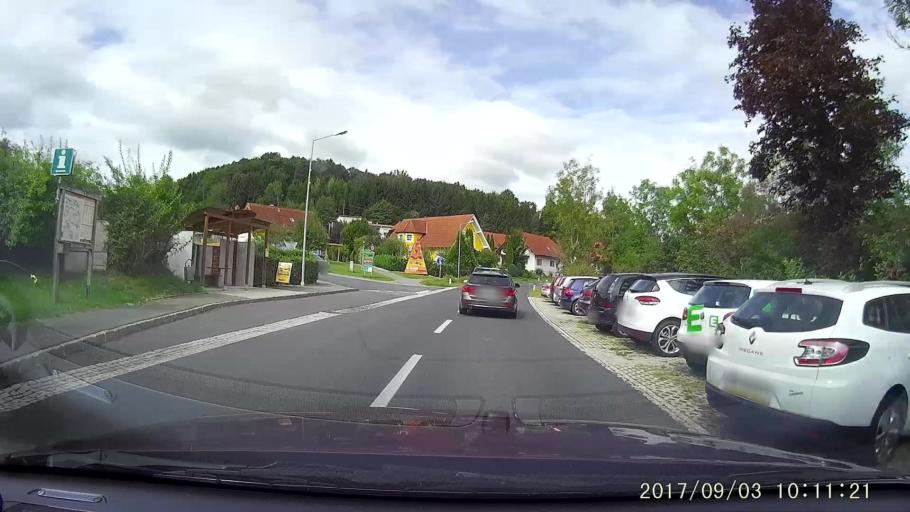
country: AT
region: Styria
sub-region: Politischer Bezirk Suedoststeiermark
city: Auersbach
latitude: 46.9934
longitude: 15.8697
